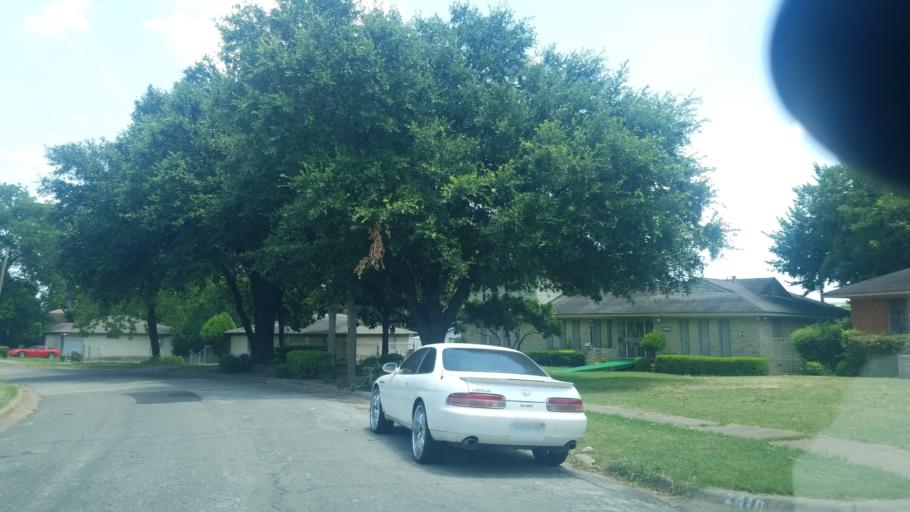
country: US
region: Texas
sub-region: Dallas County
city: Dallas
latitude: 32.7188
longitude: -96.7833
